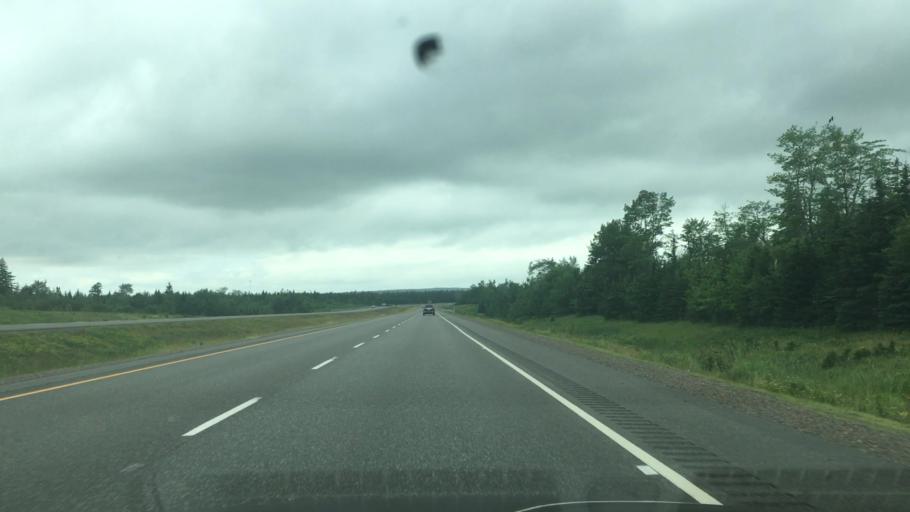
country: CA
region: Nova Scotia
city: Truro
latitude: 45.4312
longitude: -63.5602
